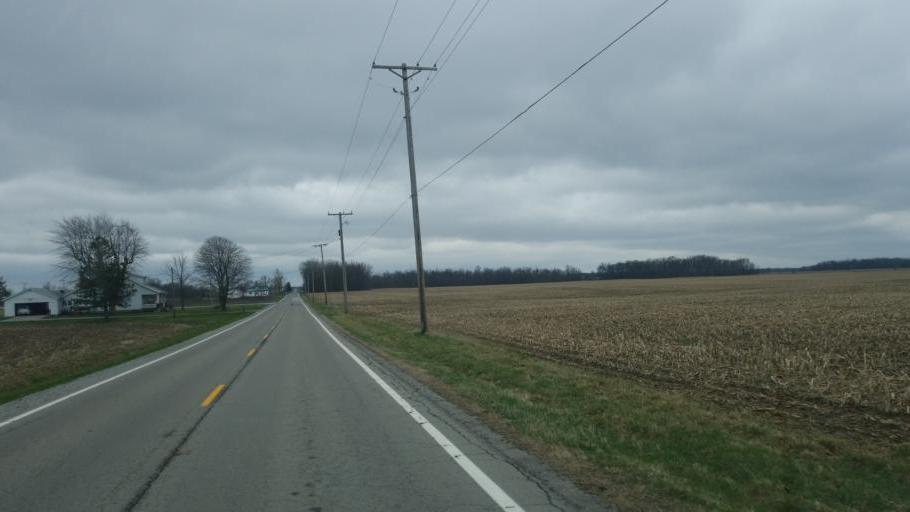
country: US
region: Ohio
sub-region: Hardin County
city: Kenton
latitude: 40.7014
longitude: -83.5751
